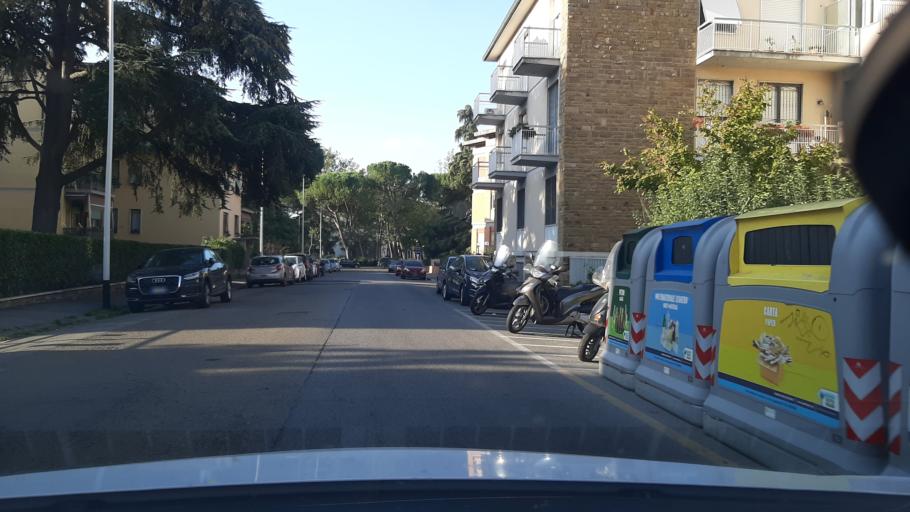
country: IT
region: Tuscany
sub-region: Province of Florence
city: Fiesole
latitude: 43.7840
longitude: 11.2928
